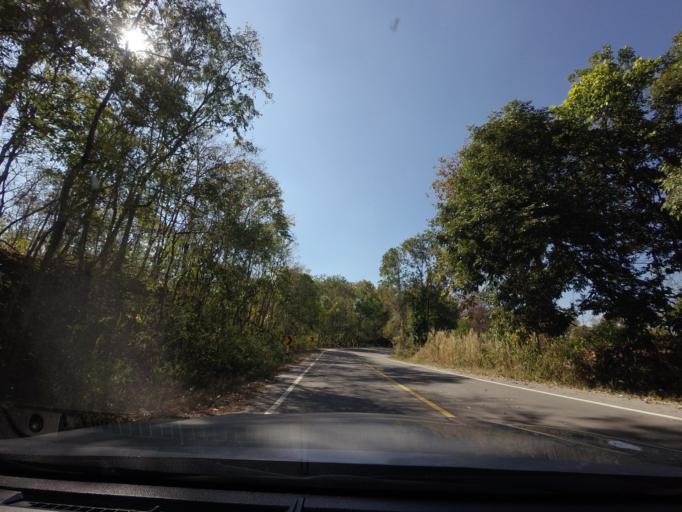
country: TH
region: Lampang
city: Chae Hom
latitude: 18.6515
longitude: 99.6031
